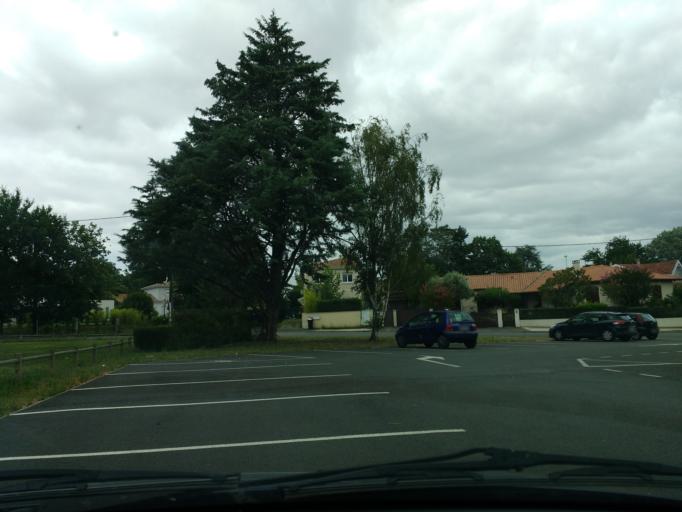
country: FR
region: Aquitaine
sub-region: Departement de la Gironde
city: Gradignan
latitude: 44.7797
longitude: -0.6027
